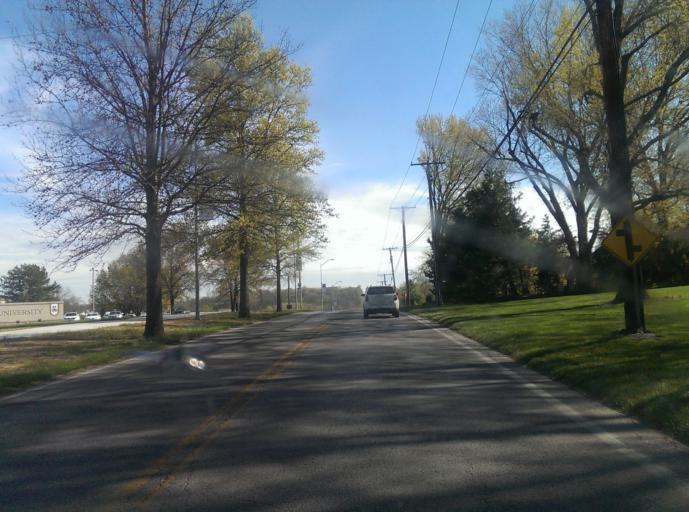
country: US
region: Kansas
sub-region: Johnson County
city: Leawood
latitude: 38.9144
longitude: -94.5935
